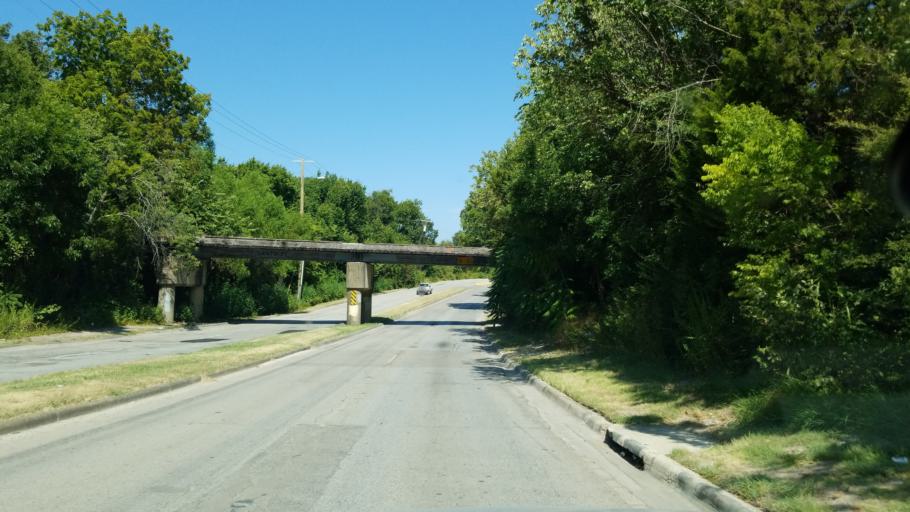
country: US
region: Texas
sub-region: Dallas County
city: Cockrell Hill
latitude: 32.7374
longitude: -96.8972
